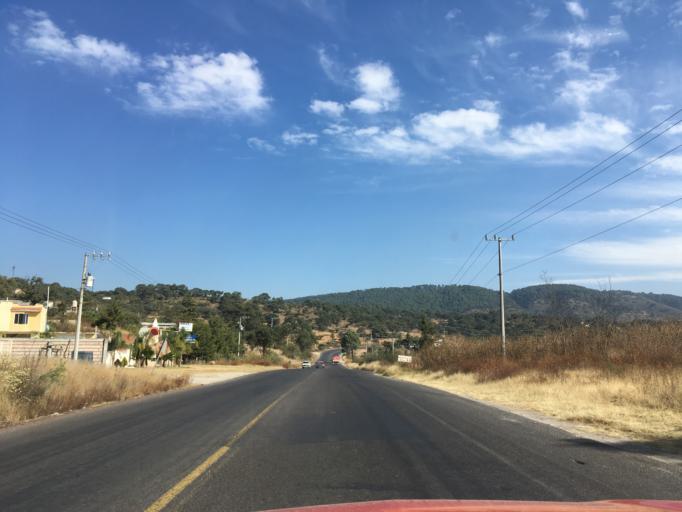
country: MX
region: Michoacan
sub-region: Hidalgo
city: Rincon de Cedenos (Rincon de Dolores)
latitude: 19.6990
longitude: -100.5800
